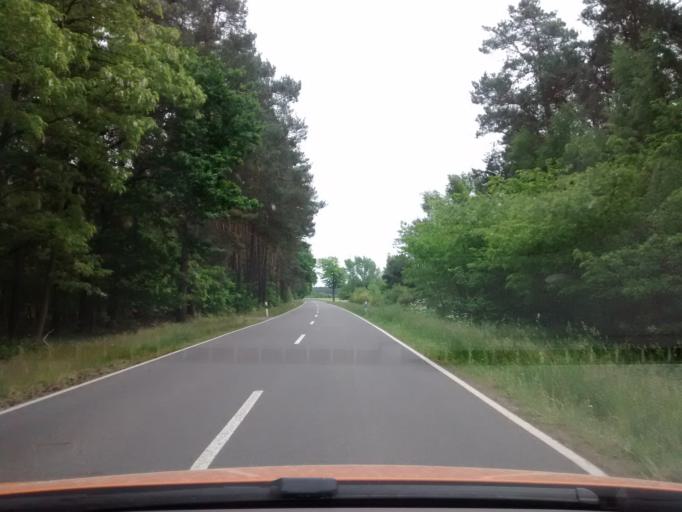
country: DE
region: Saxony-Anhalt
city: Holzdorf
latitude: 51.8339
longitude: 13.1874
